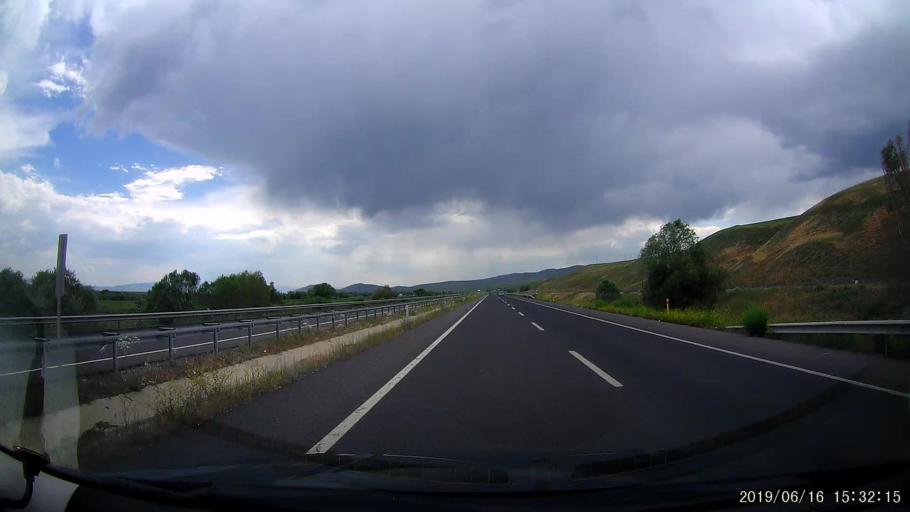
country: TR
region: Erzurum
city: Horasan
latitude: 40.0300
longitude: 42.0534
